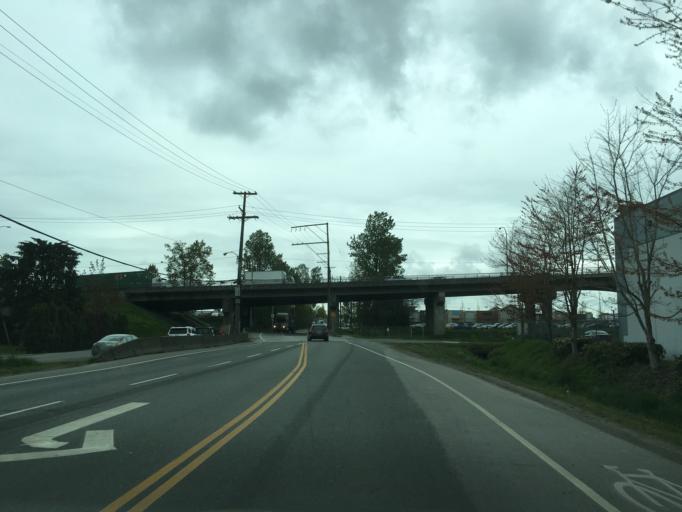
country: CA
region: British Columbia
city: New Westminster
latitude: 49.1931
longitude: -122.9417
